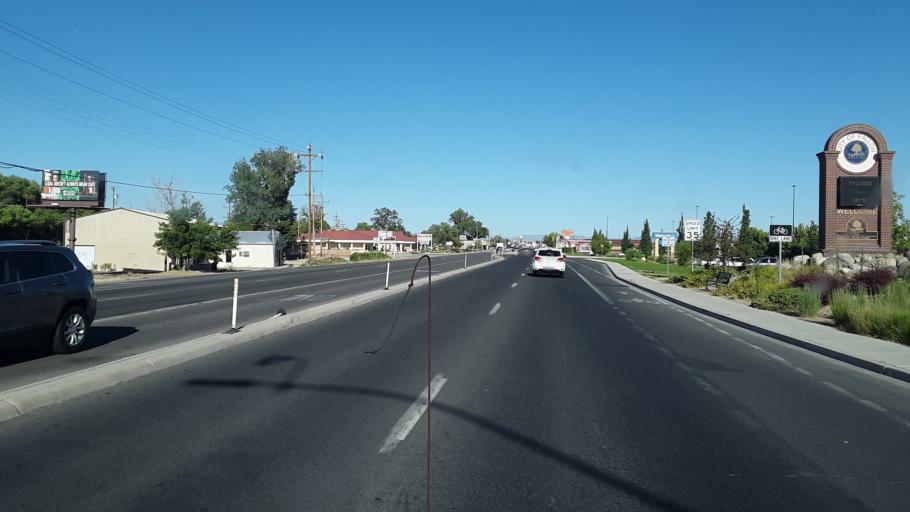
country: US
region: Nevada
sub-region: Churchill County
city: Fallon
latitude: 39.4782
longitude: -118.8082
